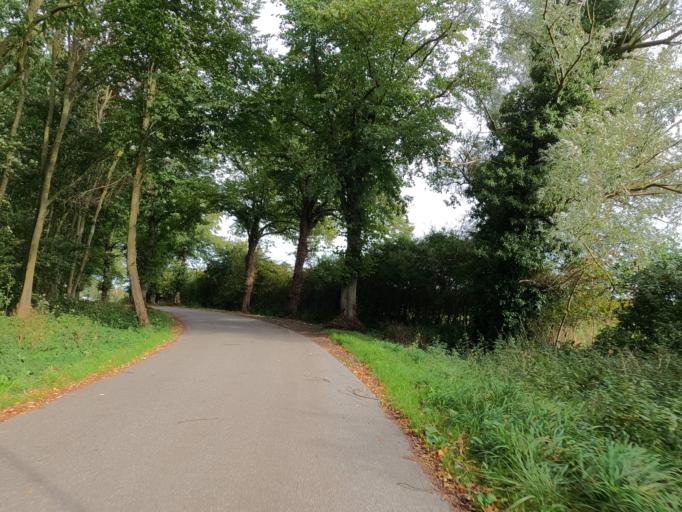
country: DE
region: Schleswig-Holstein
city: Riepsdorf
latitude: 54.1943
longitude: 11.0057
